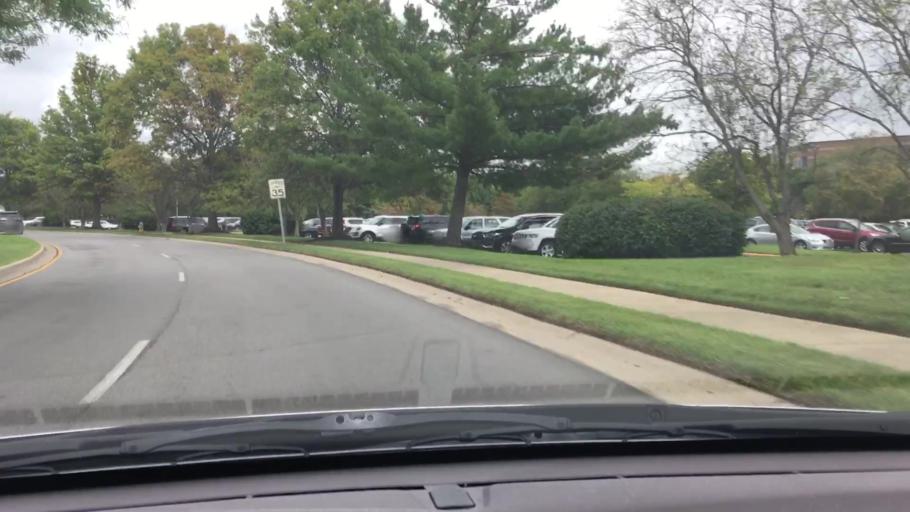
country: US
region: Kentucky
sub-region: Jefferson County
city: Beechwood Village
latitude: 38.2405
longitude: -85.6312
